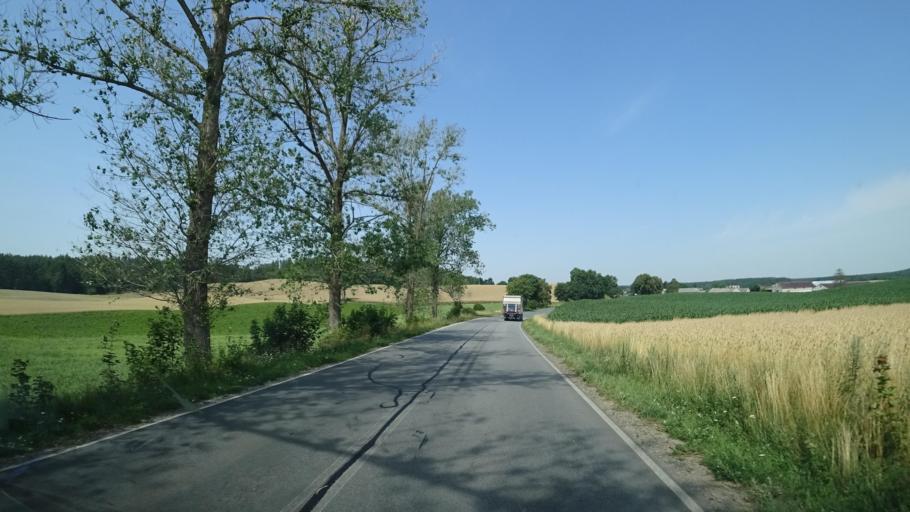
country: PL
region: Pomeranian Voivodeship
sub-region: Powiat koscierski
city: Lipusz
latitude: 54.0713
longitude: 17.8032
